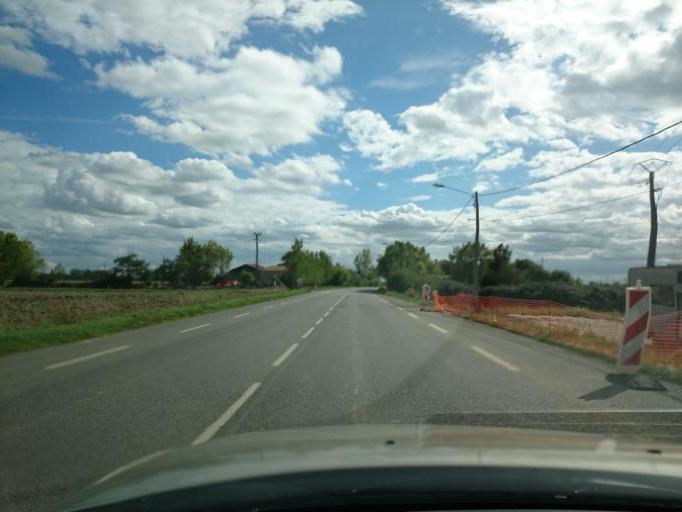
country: FR
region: Aquitaine
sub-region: Departement de la Gironde
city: Saint-Louis-de-Montferrand
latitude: 44.9281
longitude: -0.5624
